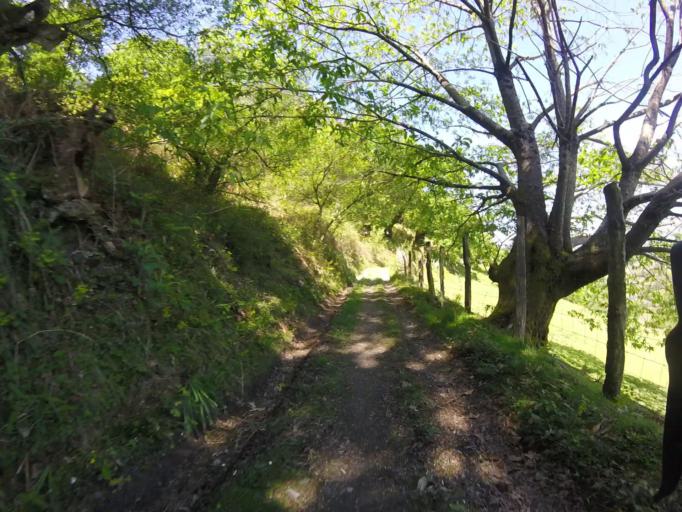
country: ES
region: Navarre
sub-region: Provincia de Navarra
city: Lesaka
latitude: 43.2446
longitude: -1.7489
